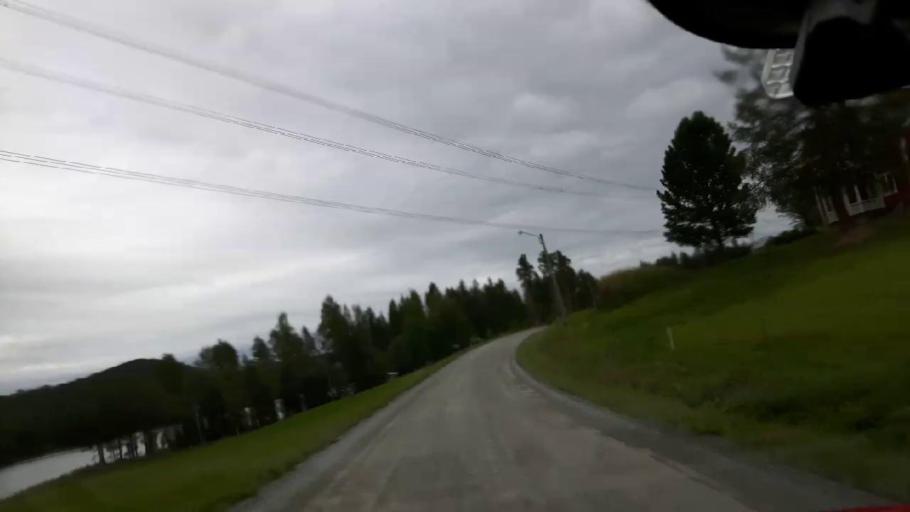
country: SE
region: Jaemtland
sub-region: Braecke Kommun
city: Braecke
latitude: 63.0811
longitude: 15.2840
